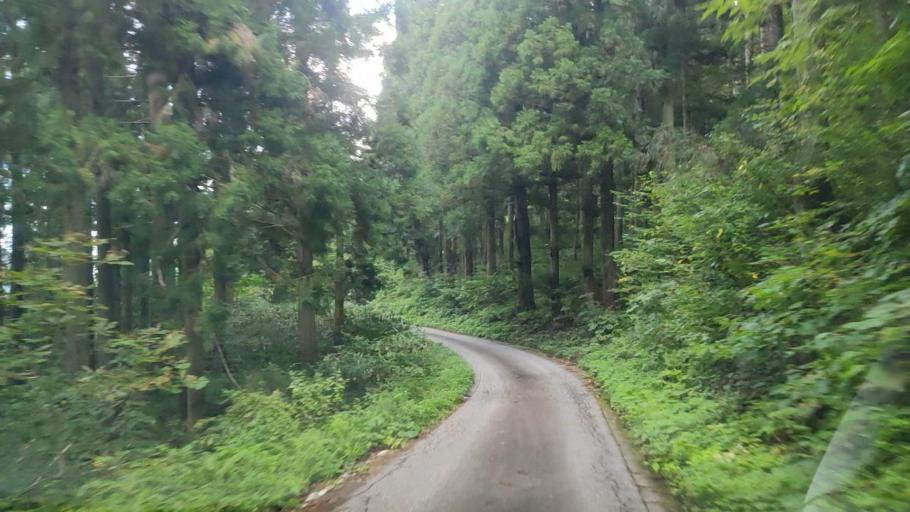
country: JP
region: Toyama
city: Yatsuomachi-higashikumisaka
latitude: 36.4115
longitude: 137.0790
